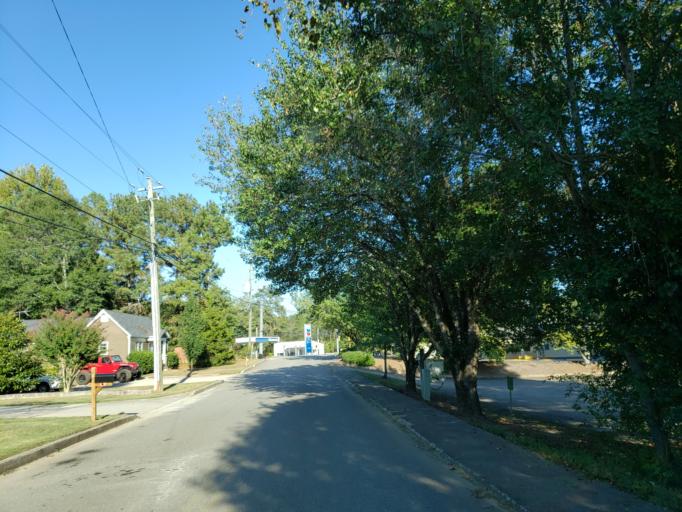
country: US
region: Georgia
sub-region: Cherokee County
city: Ball Ground
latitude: 34.3404
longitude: -84.3828
